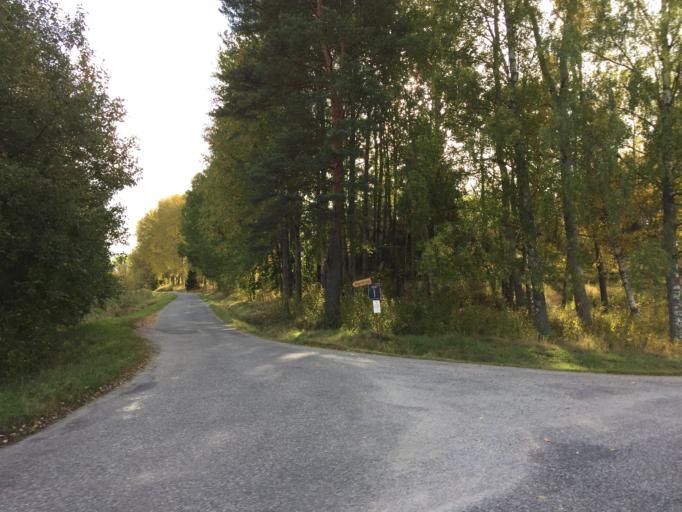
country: SE
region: Stockholm
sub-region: Sodertalje Kommun
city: Soedertaelje
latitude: 59.1494
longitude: 17.5996
